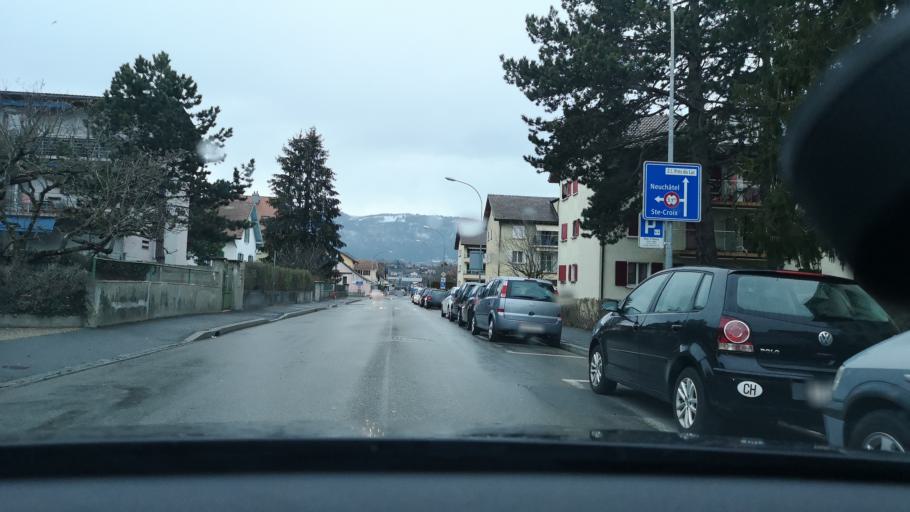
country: CH
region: Vaud
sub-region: Jura-Nord vaudois District
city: Yverdon-les-Bains
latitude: 46.7883
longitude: 6.6339
